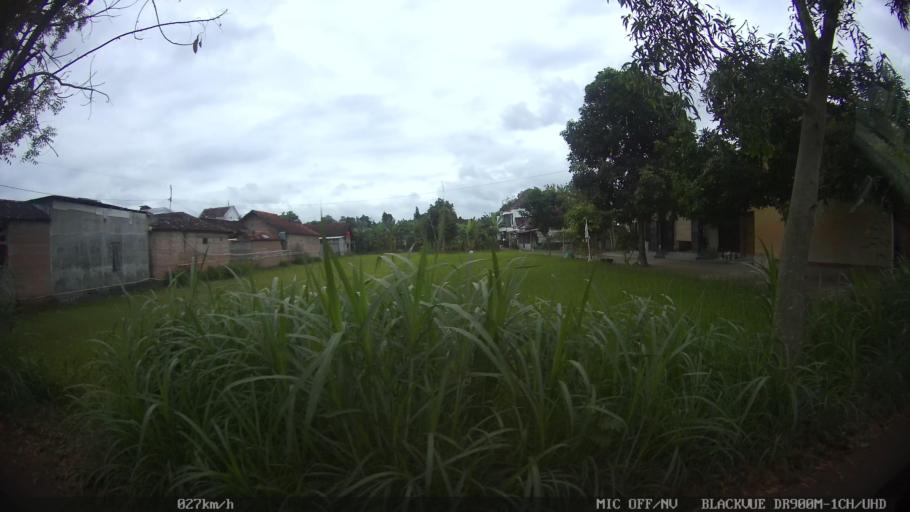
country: ID
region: Daerah Istimewa Yogyakarta
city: Sewon
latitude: -7.8443
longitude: 110.3991
